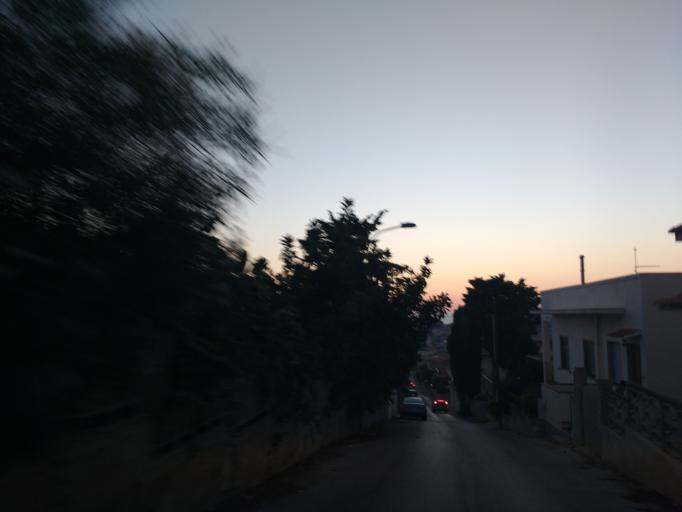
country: IT
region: Sicily
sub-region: Ragusa
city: Cava d'Aliga
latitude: 36.7288
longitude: 14.6900
